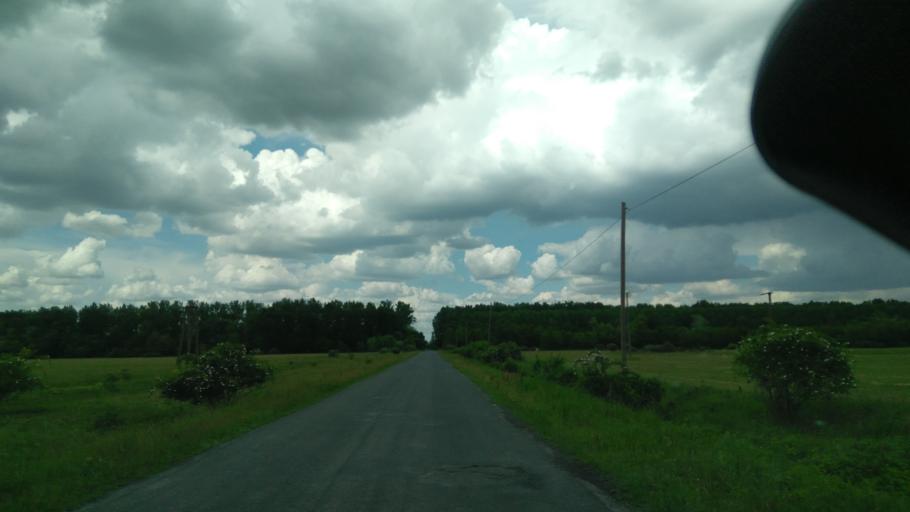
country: HU
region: Bekes
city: Szeghalom
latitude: 47.1139
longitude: 21.0882
